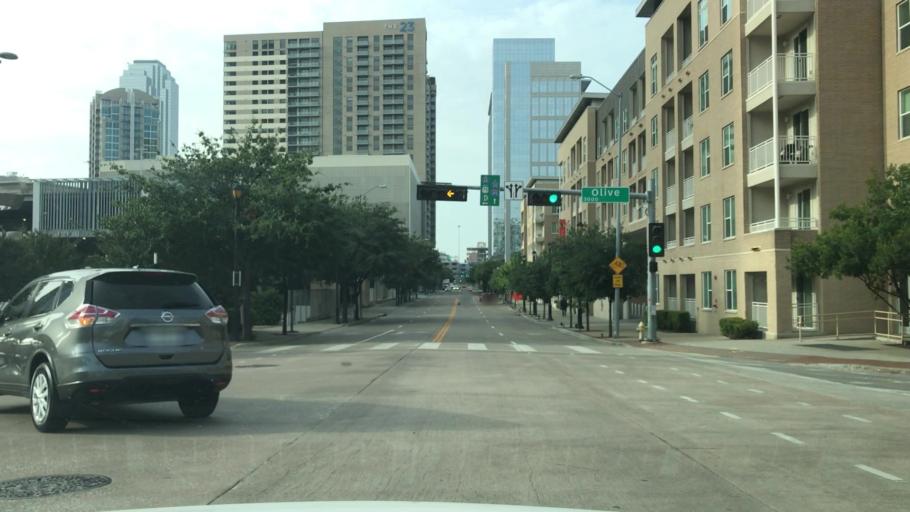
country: US
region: Texas
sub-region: Dallas County
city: Dallas
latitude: 32.7889
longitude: -96.8110
